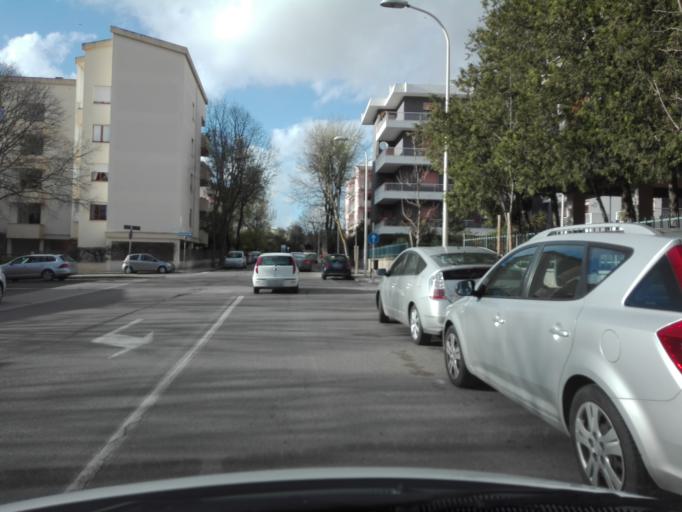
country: IT
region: Sardinia
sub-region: Provincia di Sassari
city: Sassari
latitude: 40.7217
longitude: 8.5817
